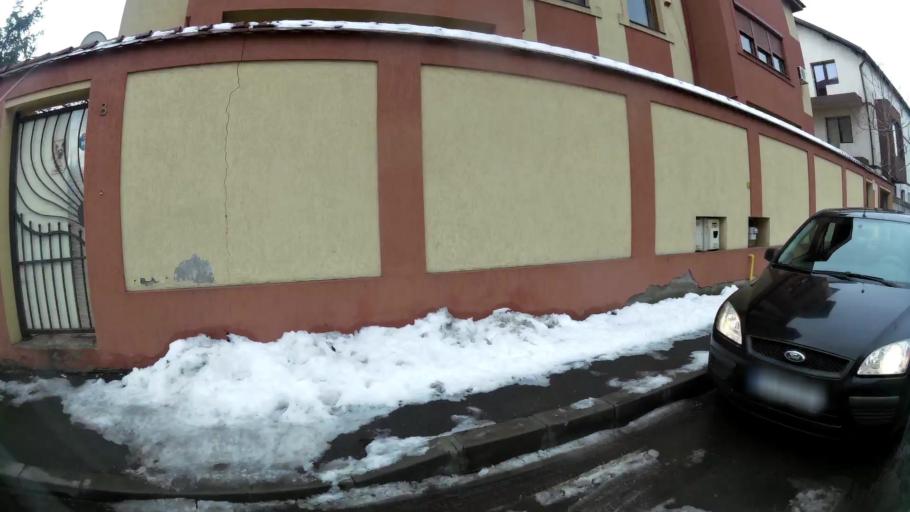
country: RO
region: Bucuresti
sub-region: Municipiul Bucuresti
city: Bucharest
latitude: 44.4092
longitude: 26.1297
